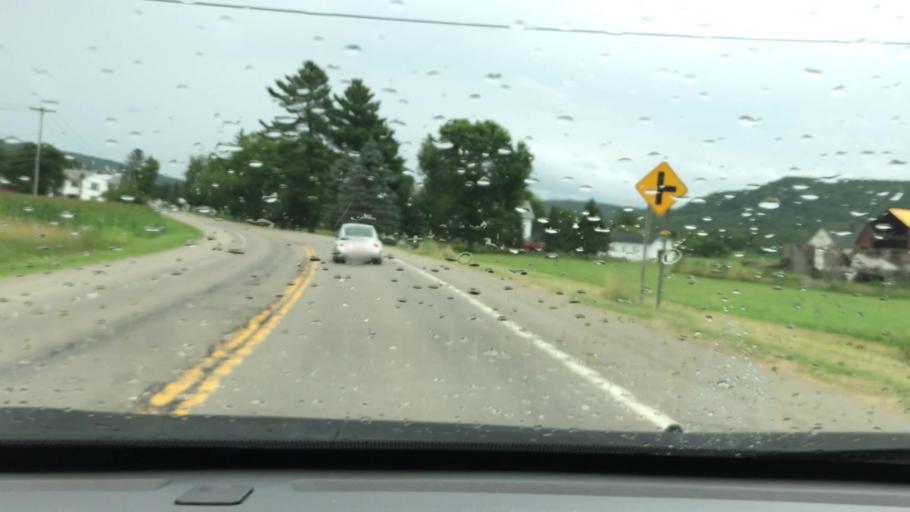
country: US
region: New York
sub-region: Cattaraugus County
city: Salamanca
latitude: 42.1937
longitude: -78.6615
